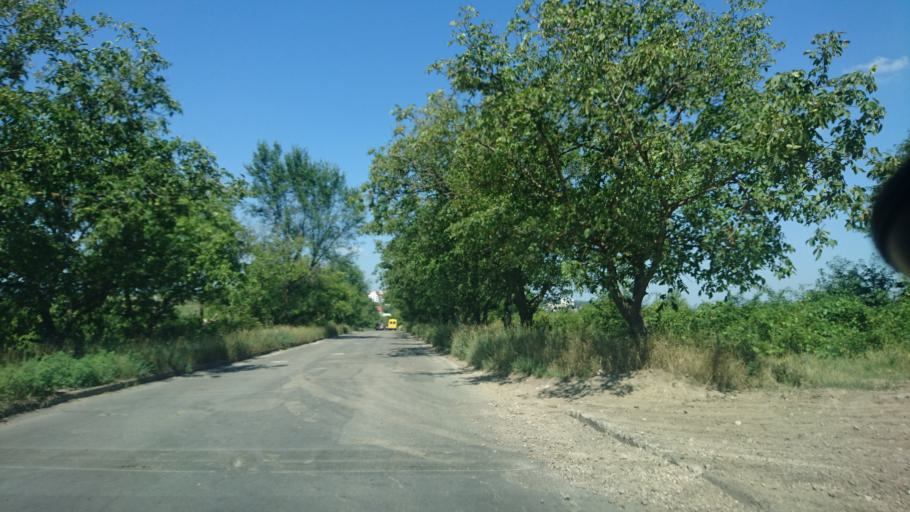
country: MD
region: Laloveni
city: Ialoveni
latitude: 47.0026
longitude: 28.7745
